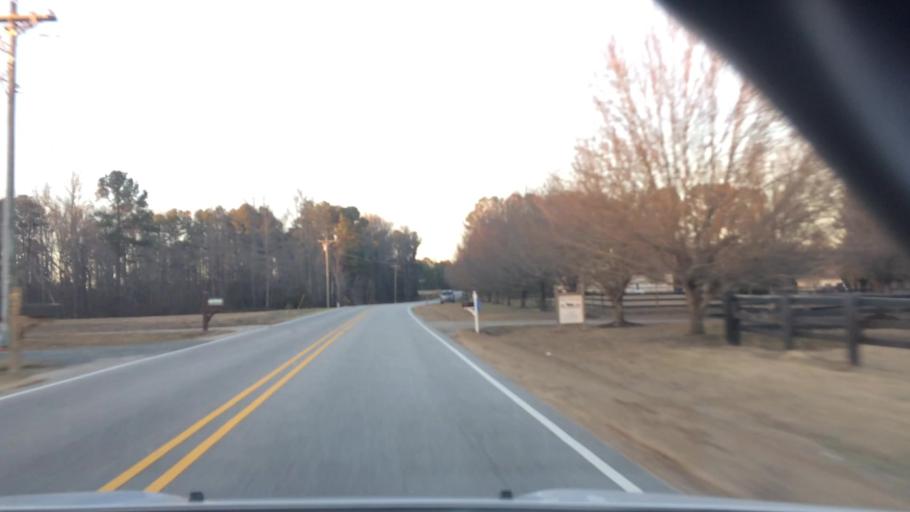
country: US
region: North Carolina
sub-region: Franklin County
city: Youngsville
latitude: 35.9921
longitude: -78.4181
